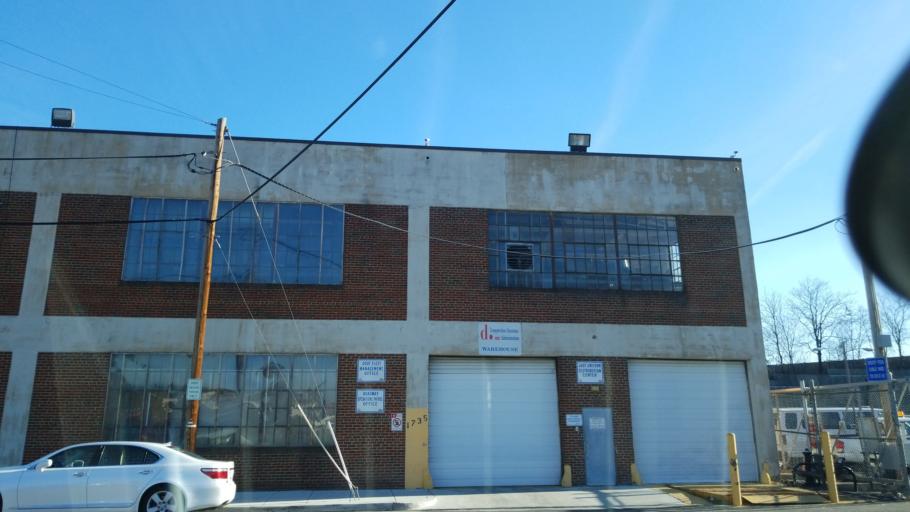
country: US
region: Maryland
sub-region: Prince George's County
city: Mount Rainier
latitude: 38.9125
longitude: -76.9813
